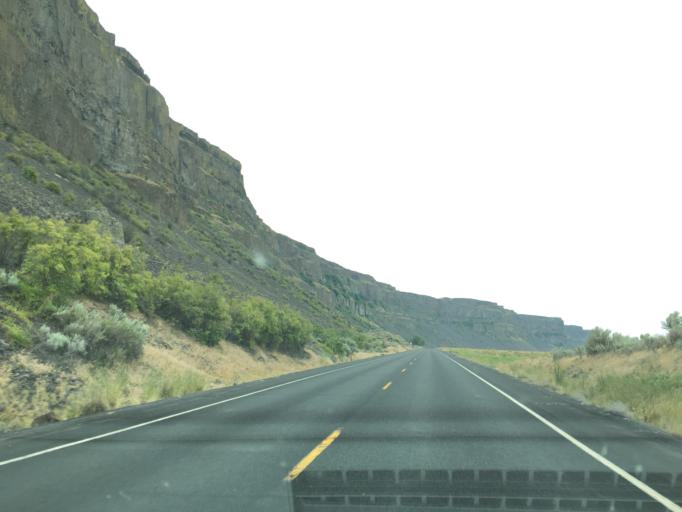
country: US
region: Washington
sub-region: Okanogan County
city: Coulee Dam
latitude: 47.8381
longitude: -119.1266
